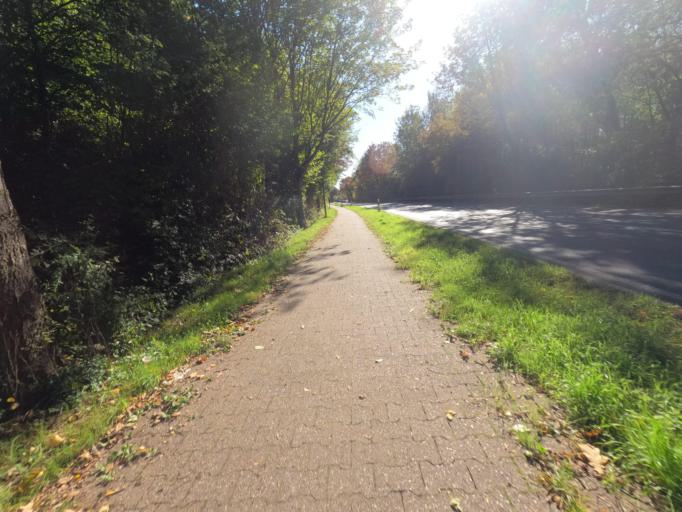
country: DE
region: North Rhine-Westphalia
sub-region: Regierungsbezirk Koln
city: Alsdorf
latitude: 50.8833
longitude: 6.1710
